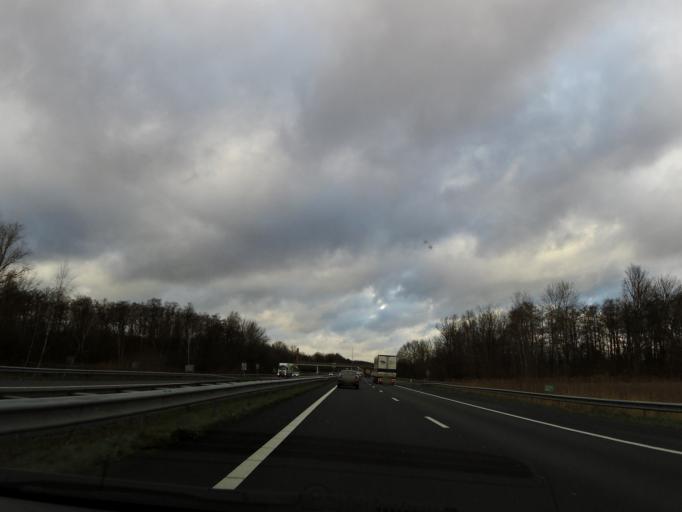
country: NL
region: Limburg
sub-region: Gemeente Venray
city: Venray
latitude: 51.5184
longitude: 6.0044
